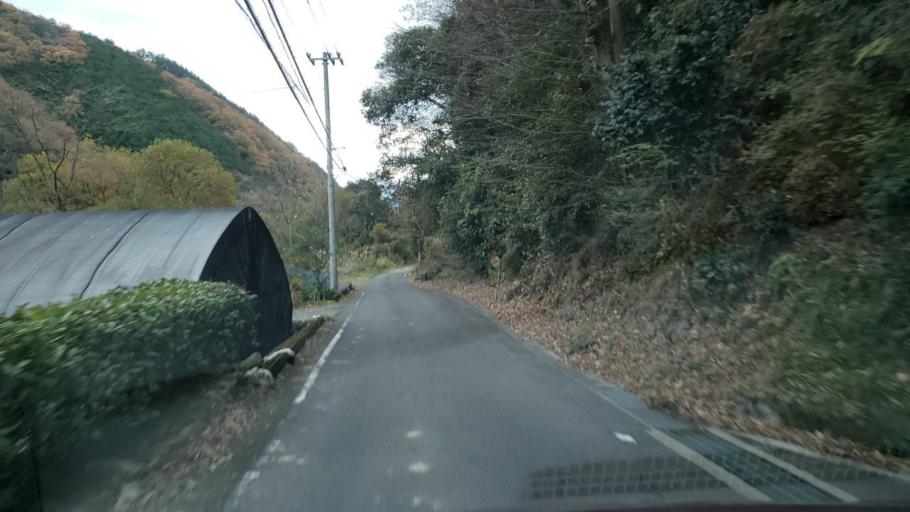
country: JP
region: Tokushima
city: Wakimachi
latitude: 34.1158
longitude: 134.2253
